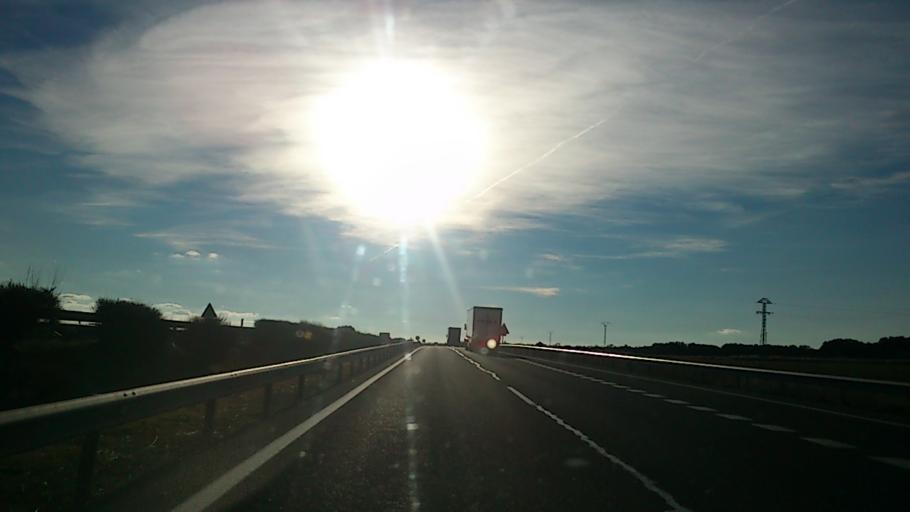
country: ES
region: Castille-La Mancha
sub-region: Provincia de Guadalajara
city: Mirabueno
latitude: 40.9267
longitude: -2.7188
